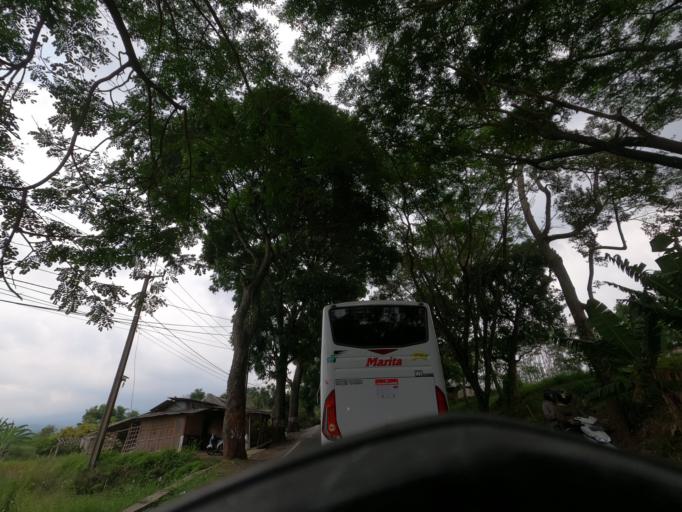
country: ID
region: West Java
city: Ciranjang-hilir
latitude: -6.7906
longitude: 107.0695
